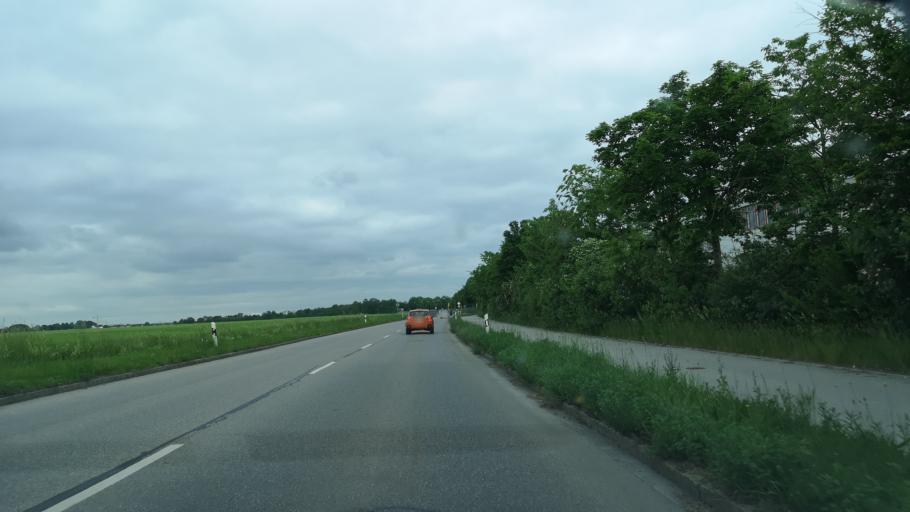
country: DE
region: Bavaria
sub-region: Upper Bavaria
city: Kirchheim bei Muenchen
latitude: 48.1551
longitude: 11.7628
